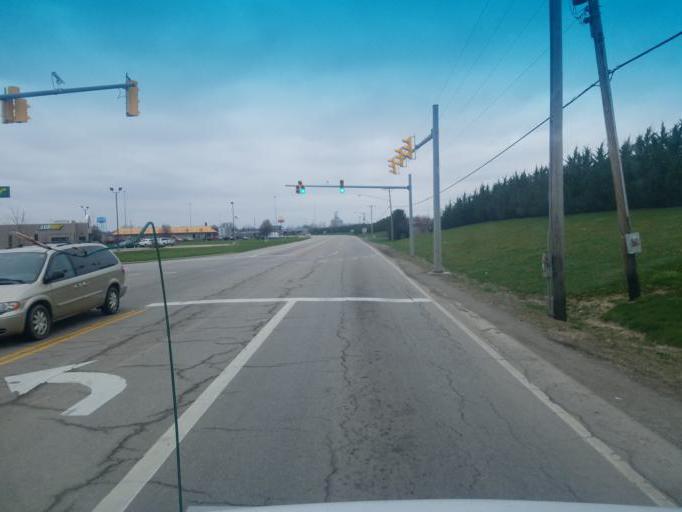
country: US
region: Ohio
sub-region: Van Wert County
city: Van Wert
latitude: 40.8906
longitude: -84.5813
